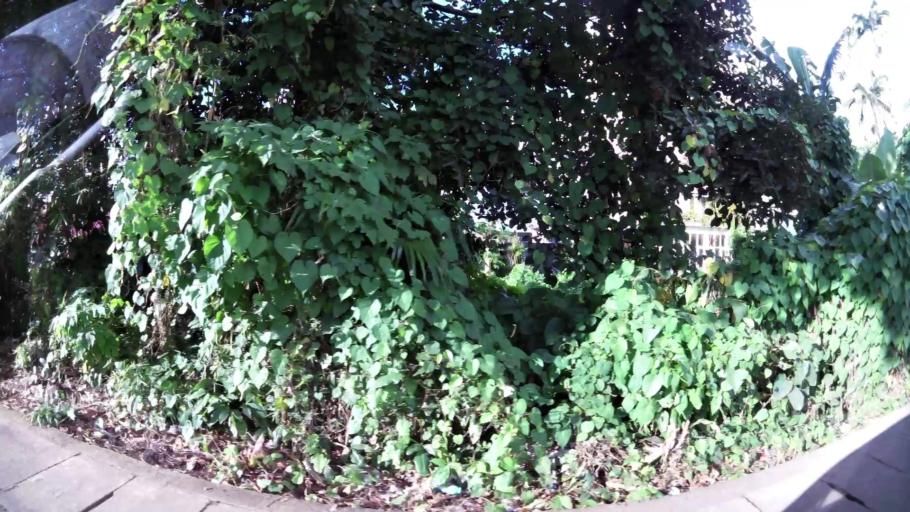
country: MU
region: Plaines Wilhems
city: Curepipe
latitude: -20.3110
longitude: 57.5134
